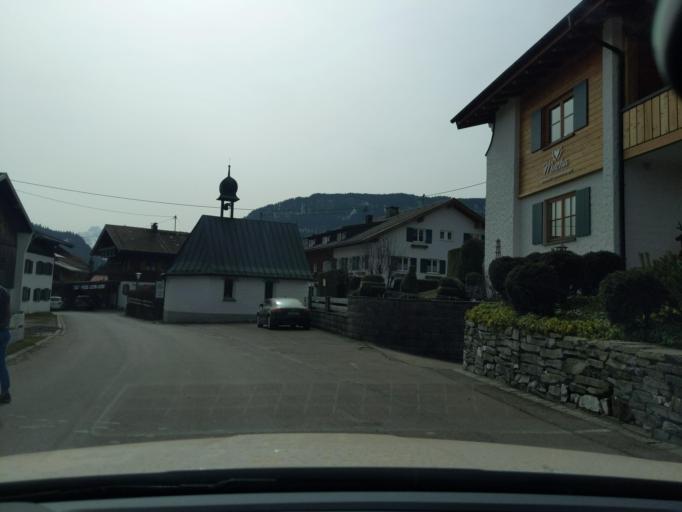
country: DE
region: Bavaria
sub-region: Swabia
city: Obermaiselstein
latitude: 47.4552
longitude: 10.2315
